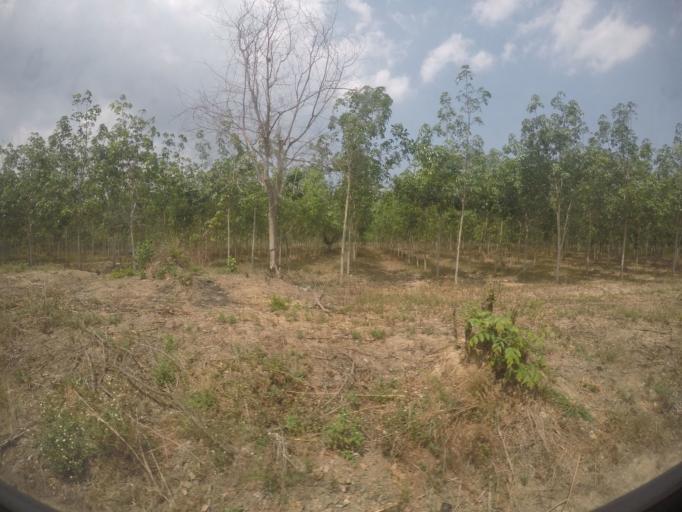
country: VN
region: Binh Thuan
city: Tanh Linh
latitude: 10.9011
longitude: 107.6914
